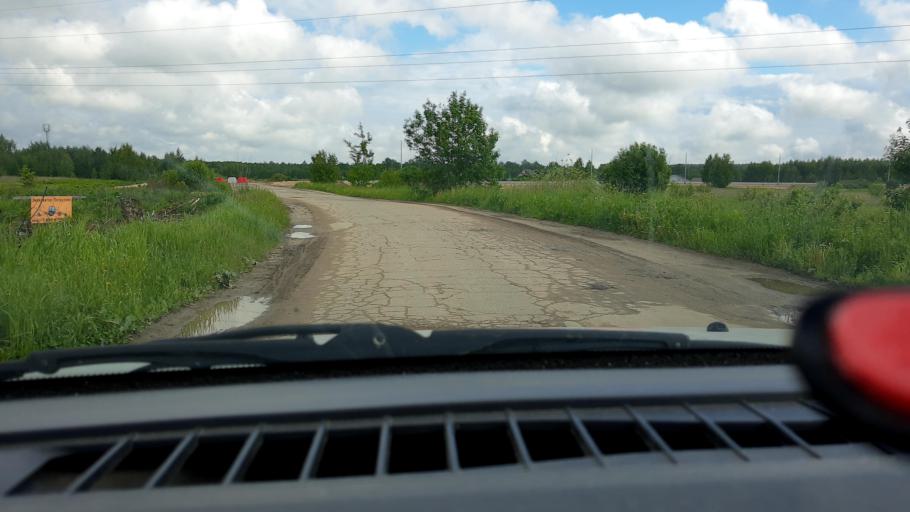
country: RU
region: Nizjnij Novgorod
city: Neklyudovo
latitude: 56.4262
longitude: 43.9637
